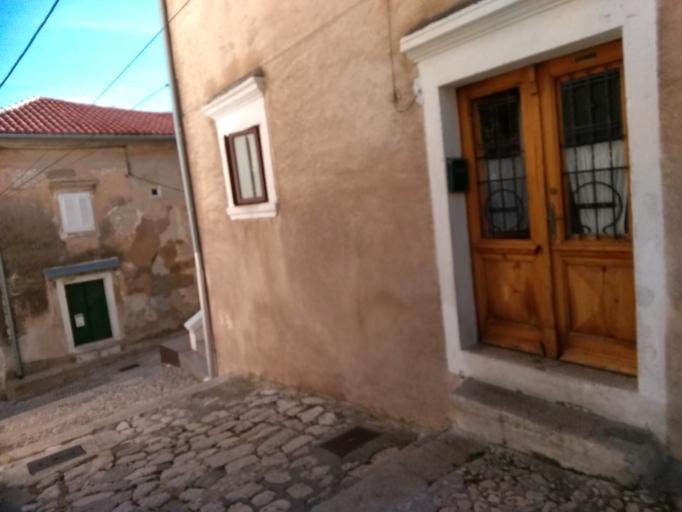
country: HR
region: Primorsko-Goranska
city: Bakar
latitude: 45.3069
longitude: 14.5340
